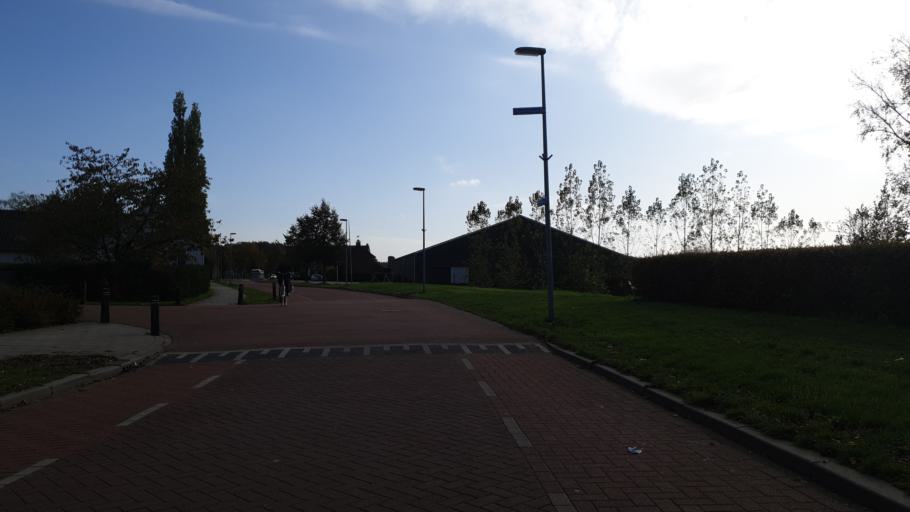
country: NL
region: Limburg
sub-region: Gemeente Gennep
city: Gennep
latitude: 51.6709
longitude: 5.9784
